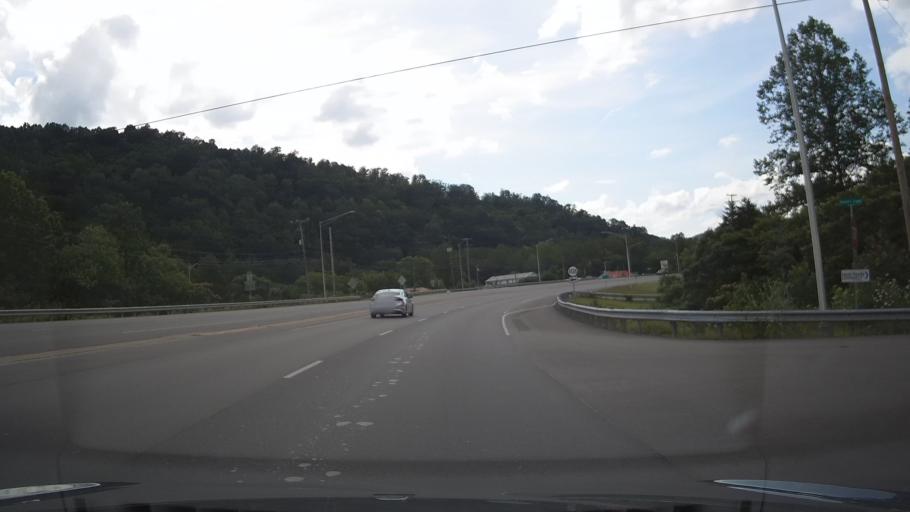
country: US
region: Kentucky
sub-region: Floyd County
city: Prestonsburg
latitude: 37.6035
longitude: -82.6983
